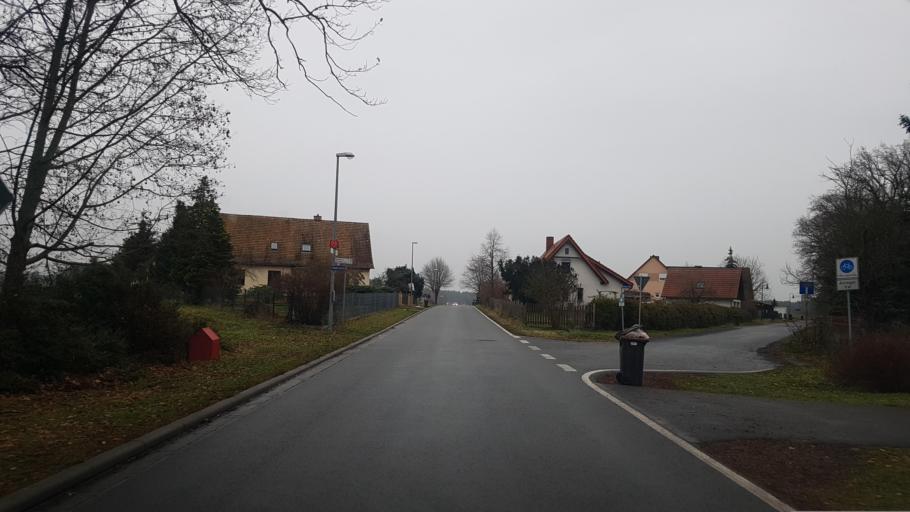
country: DE
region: Brandenburg
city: Cottbus
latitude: 51.6987
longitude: 14.3893
